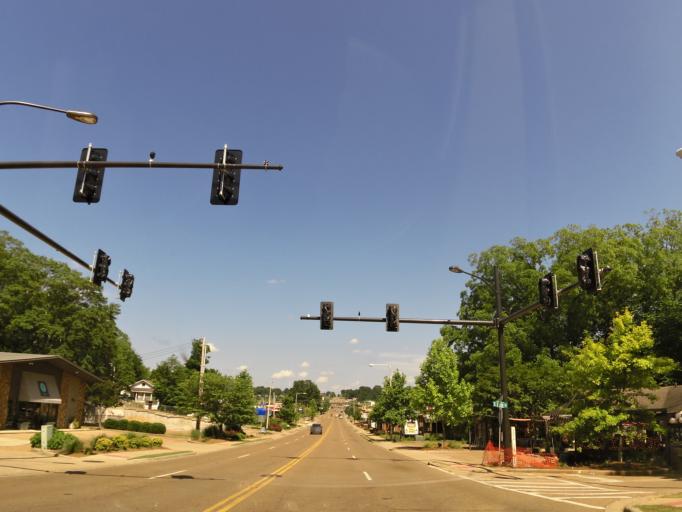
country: US
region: Mississippi
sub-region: Lafayette County
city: Oxford
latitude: 34.3633
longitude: -89.5145
